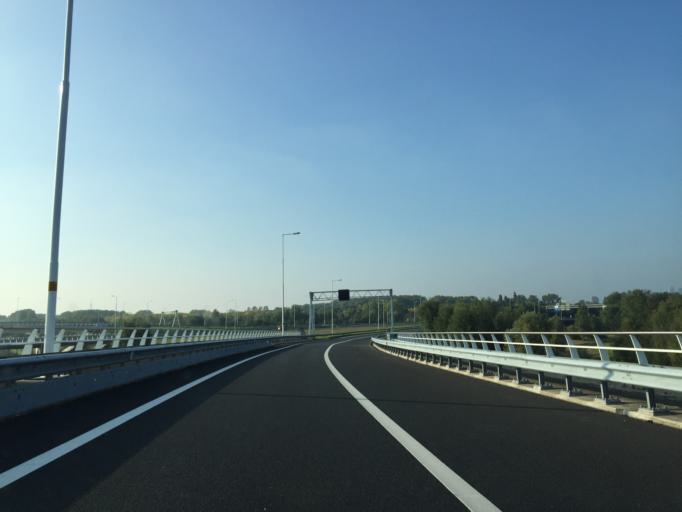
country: NL
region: South Holland
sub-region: Gemeente Barendrecht
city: Barendrecht
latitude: 51.8664
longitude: 4.5190
